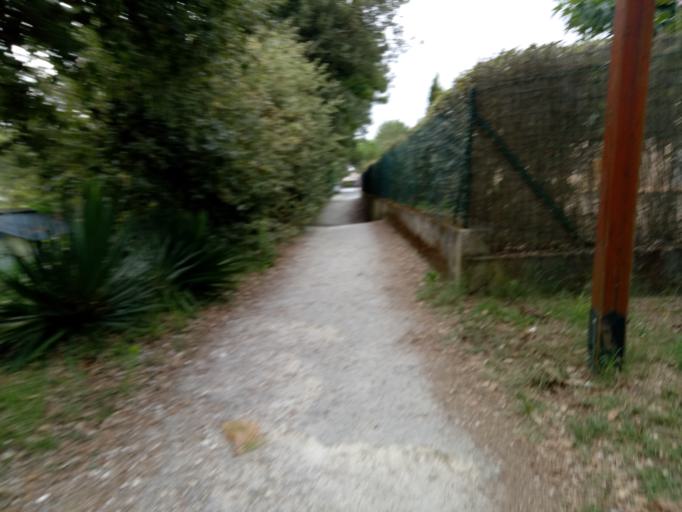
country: FR
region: Poitou-Charentes
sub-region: Departement de la Charente-Maritime
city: Saint-Trojan-les-Bains
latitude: 45.8587
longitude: -1.2366
